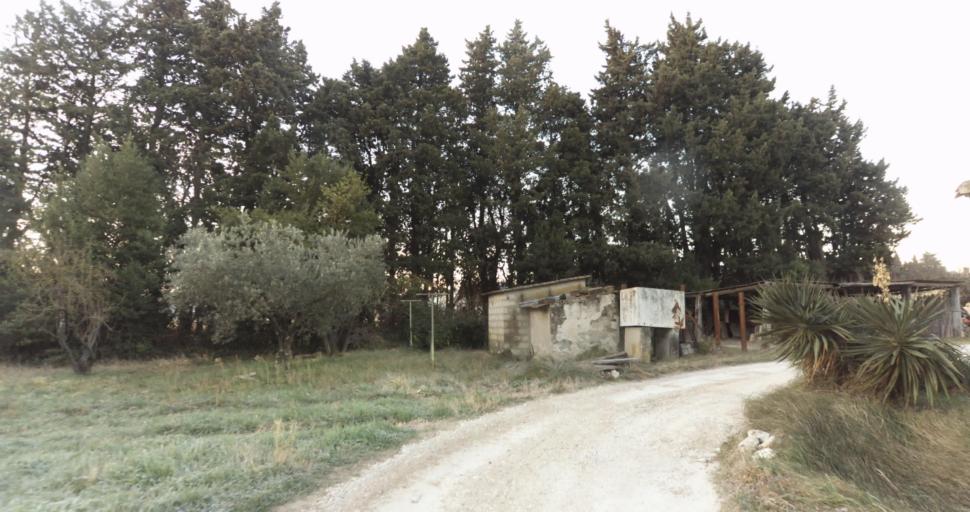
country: FR
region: Provence-Alpes-Cote d'Azur
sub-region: Departement des Bouches-du-Rhone
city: Barbentane
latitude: 43.9077
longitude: 4.7665
